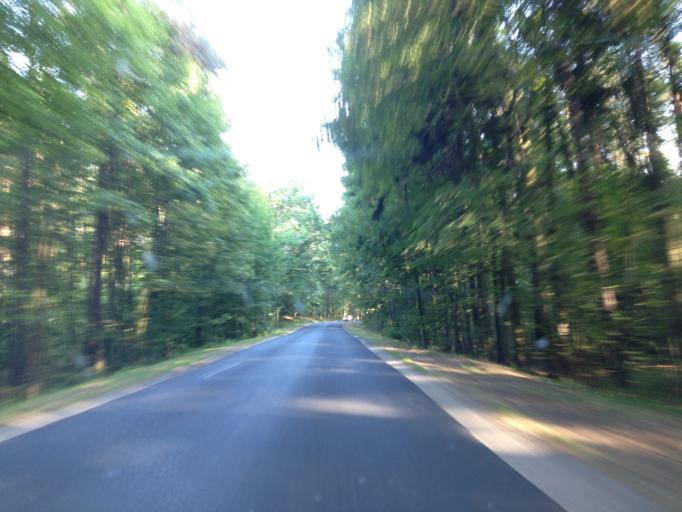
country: PL
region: Kujawsko-Pomorskie
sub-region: Powiat brodnicki
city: Brodnica
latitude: 53.3602
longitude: 19.3824
